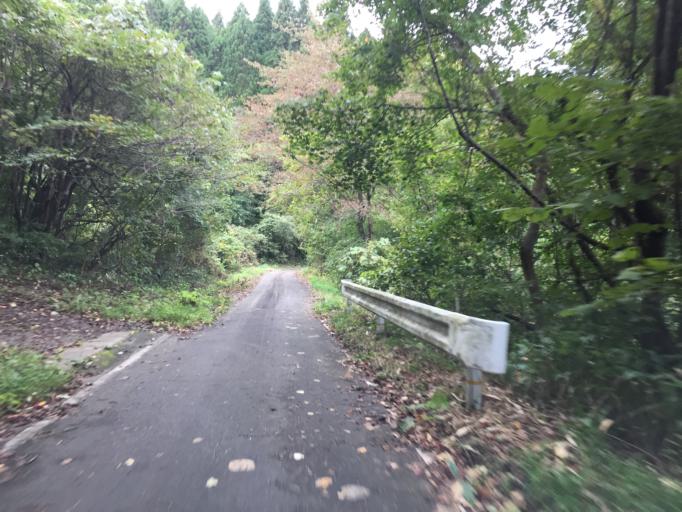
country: JP
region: Miyagi
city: Marumori
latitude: 37.9220
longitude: 140.7147
